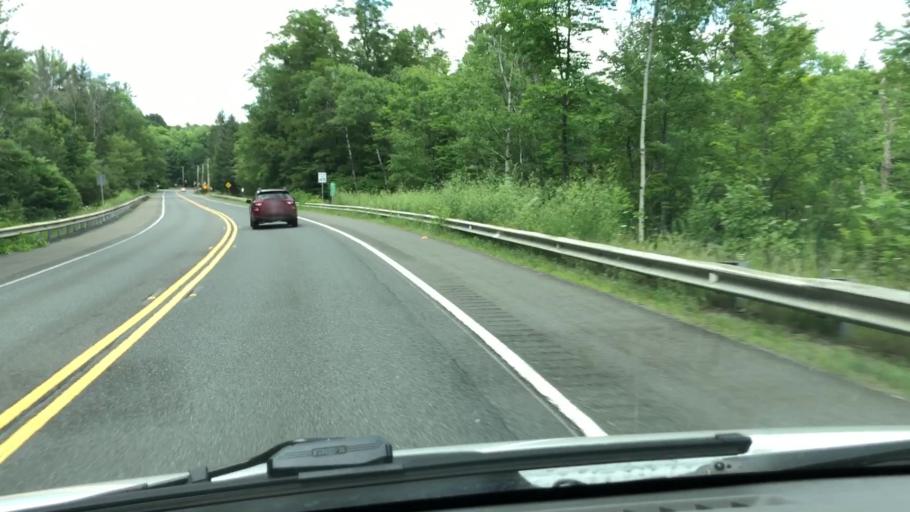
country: US
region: Massachusetts
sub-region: Hampshire County
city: Chesterfield
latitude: 42.4423
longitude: -72.8607
